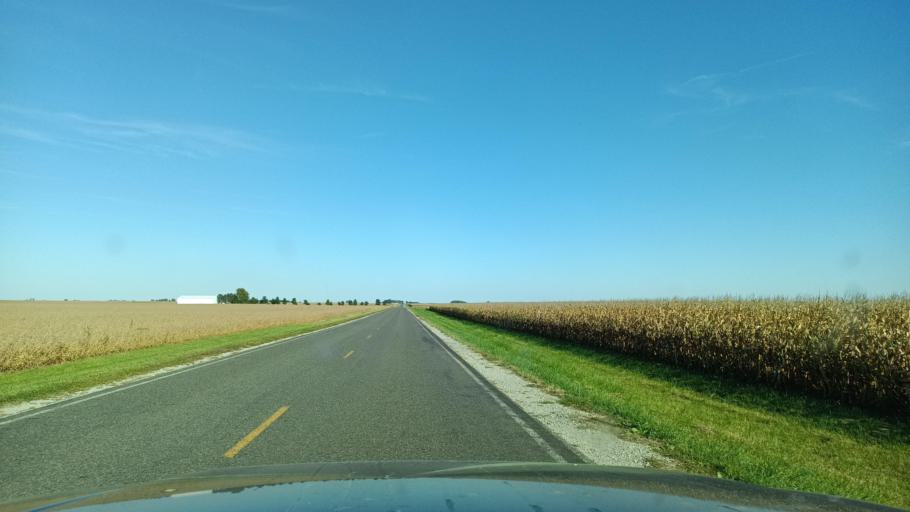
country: US
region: Illinois
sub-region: De Witt County
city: Clinton
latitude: 40.2245
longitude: -88.9545
